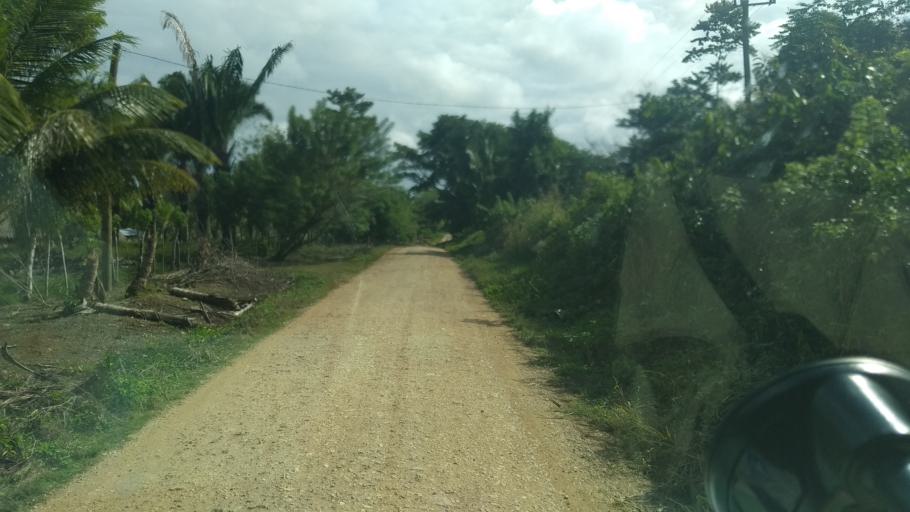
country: BZ
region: Toledo
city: Punta Gorda
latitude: 16.2072
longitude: -88.9170
